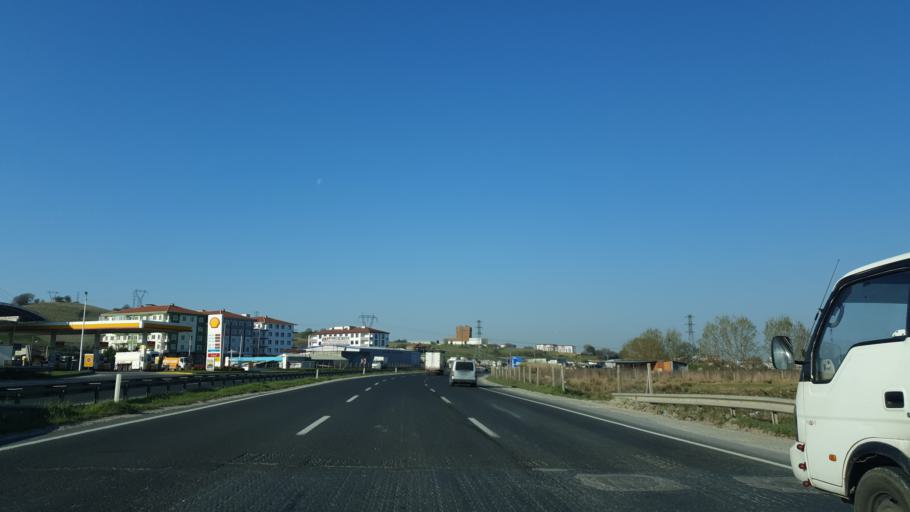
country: TR
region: Tekirdag
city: Cerkezkoey
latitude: 41.2675
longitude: 27.9562
